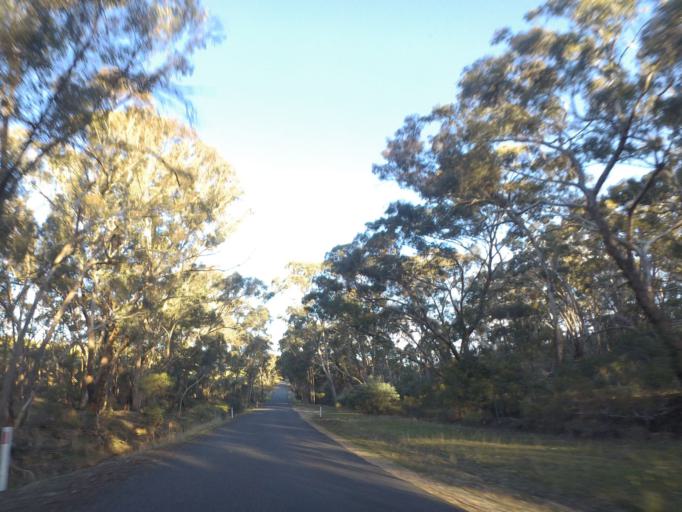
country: AU
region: Victoria
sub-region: Mount Alexander
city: Castlemaine
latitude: -37.1495
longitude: 144.2065
